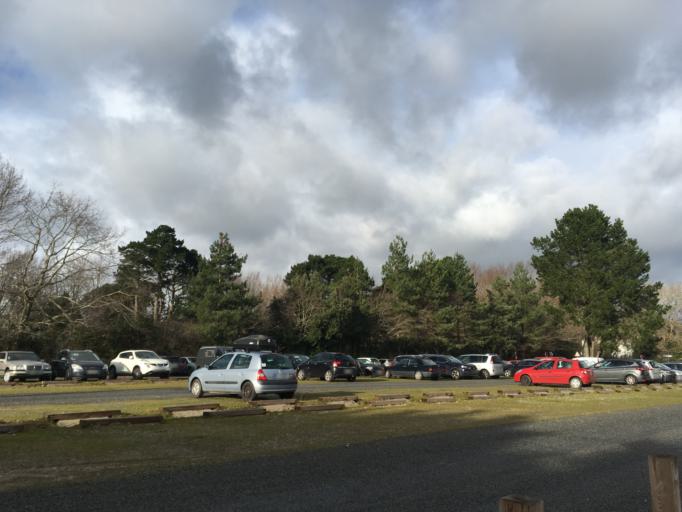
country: FR
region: Brittany
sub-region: Departement du Morbihan
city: Larmor-Baden
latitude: 47.5998
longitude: -2.8647
